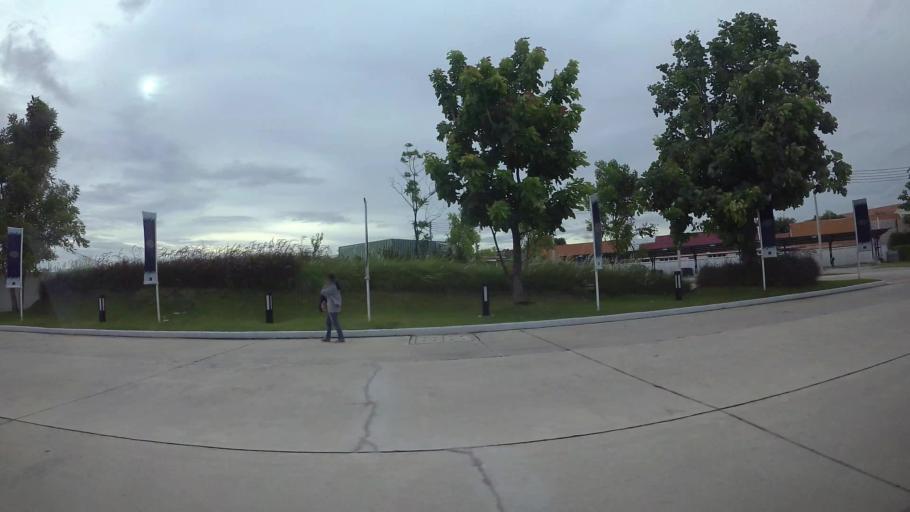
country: TH
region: Chon Buri
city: Si Racha
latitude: 13.1358
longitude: 100.9645
